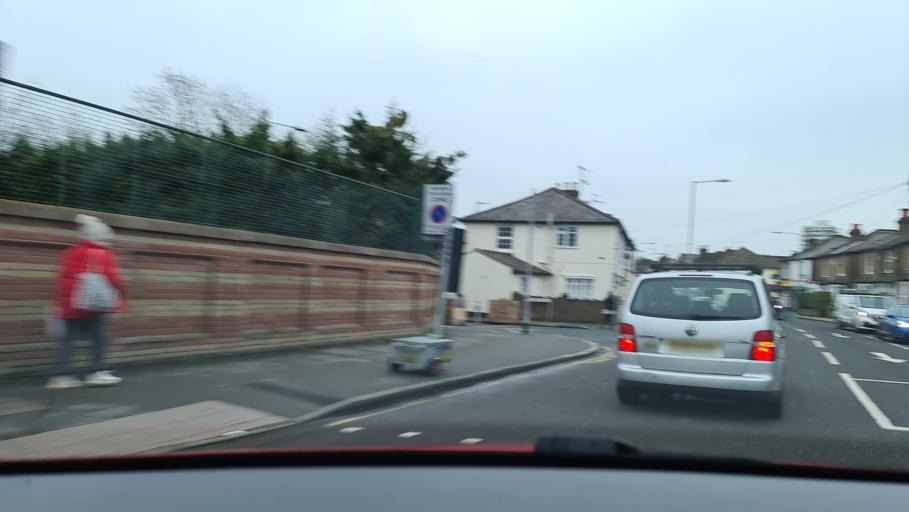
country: GB
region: England
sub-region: Greater London
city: Kingston upon Thames
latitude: 51.4080
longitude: -0.2945
